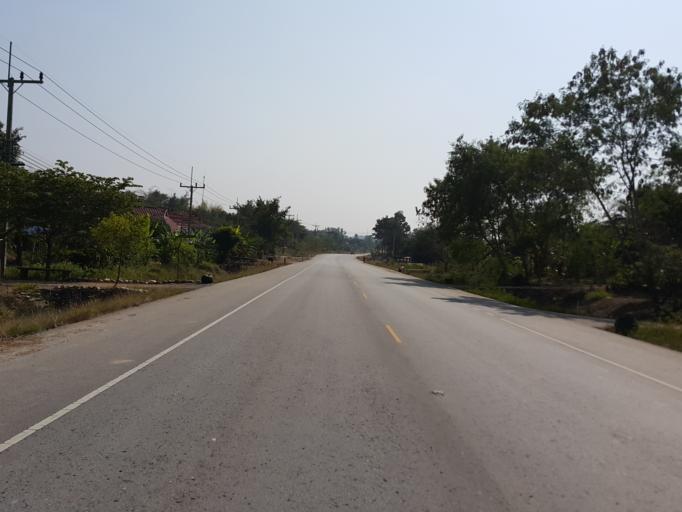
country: TH
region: Lampang
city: Mueang Pan
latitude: 18.9301
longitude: 99.6112
